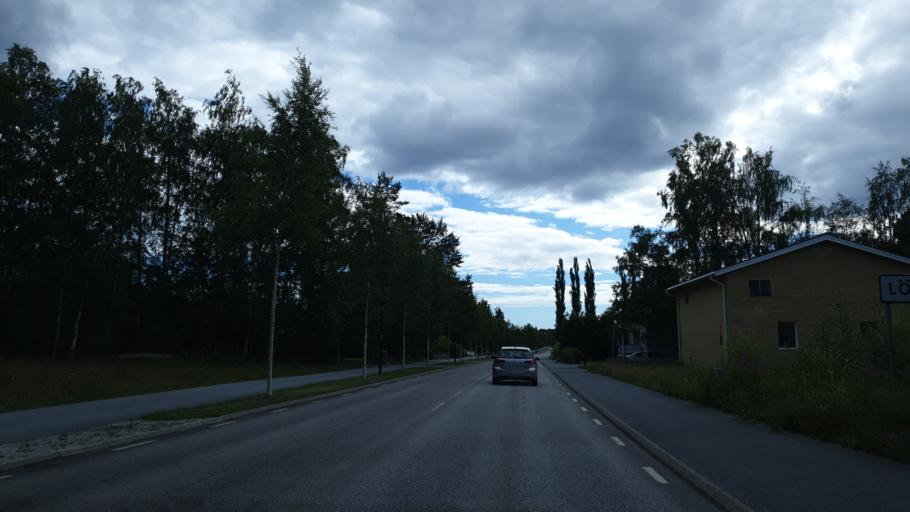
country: SE
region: Vaesterbotten
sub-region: Umea Kommun
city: Holmsund
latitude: 63.7253
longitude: 20.3899
